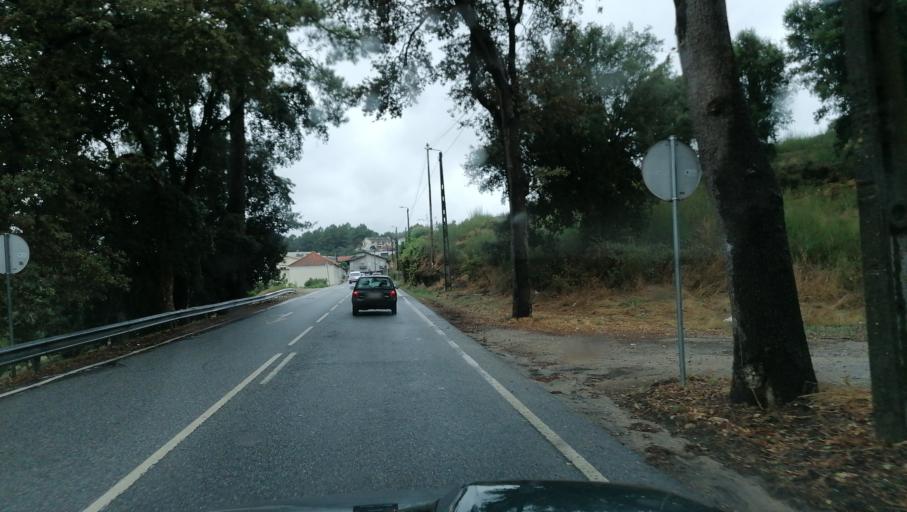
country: PT
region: Braga
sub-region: Guimaraes
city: Moreira de Conegos
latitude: 41.3872
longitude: -8.3404
